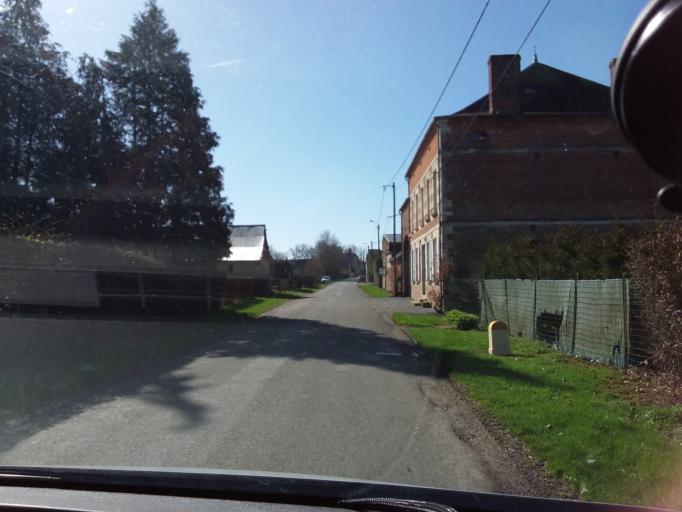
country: FR
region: Picardie
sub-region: Departement de l'Aisne
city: Montcornet
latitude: 49.7527
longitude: 4.0011
